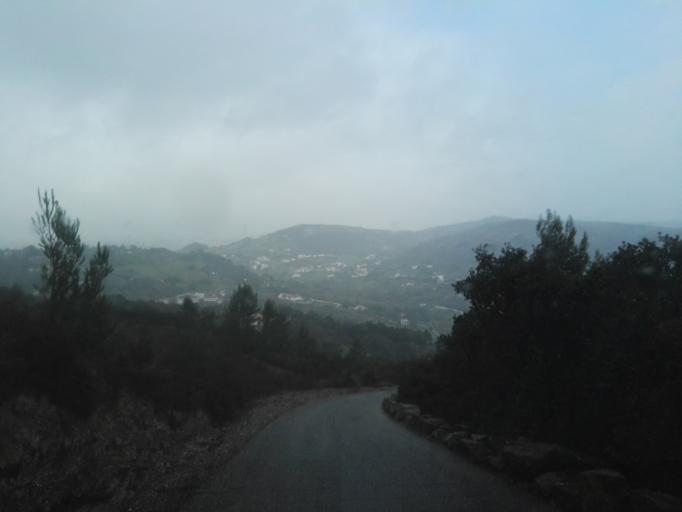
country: PT
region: Lisbon
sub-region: Vila Franca de Xira
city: Sobralinho
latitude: 38.9280
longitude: -9.0719
